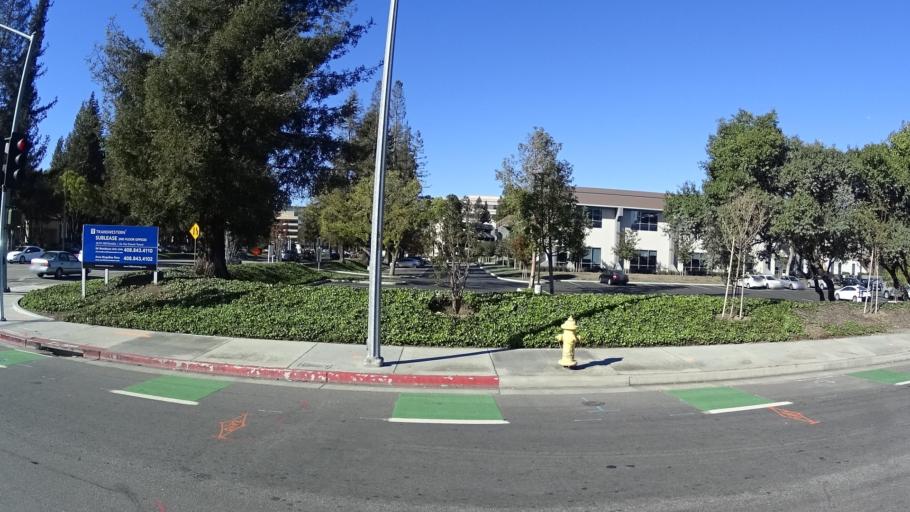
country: US
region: California
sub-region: Santa Clara County
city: San Jose
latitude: 37.3654
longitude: -121.9168
